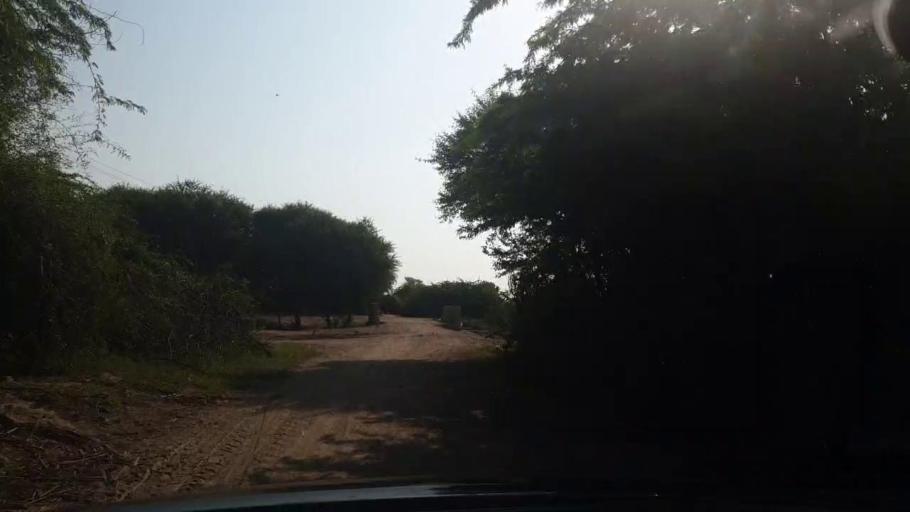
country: PK
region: Sindh
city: Tando Bago
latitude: 24.6508
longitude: 69.1742
